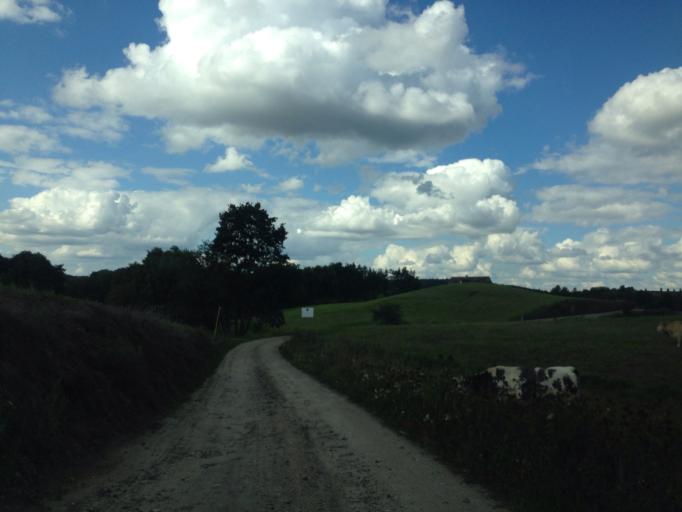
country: PL
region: Kujawsko-Pomorskie
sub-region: Powiat brodnicki
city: Gorzno
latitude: 53.2017
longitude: 19.6561
